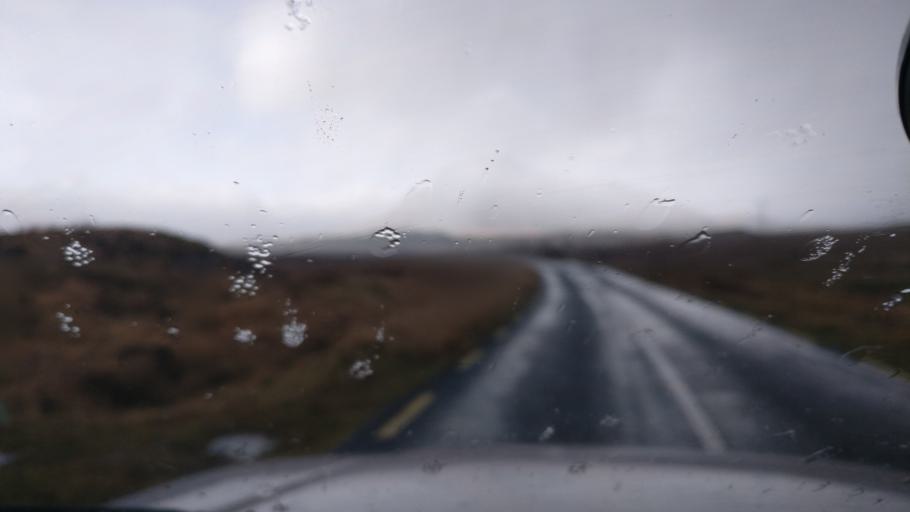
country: IE
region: Connaught
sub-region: County Galway
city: Clifden
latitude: 53.4453
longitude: -9.7694
